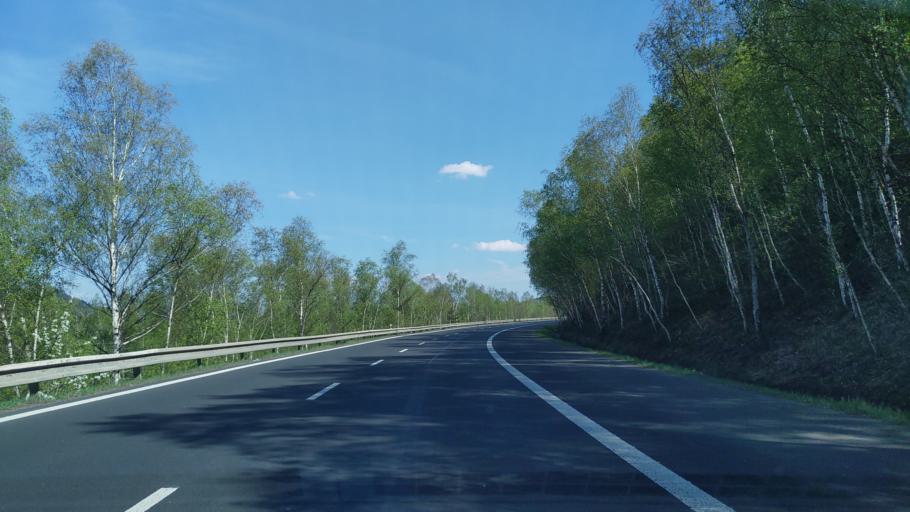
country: CZ
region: Ustecky
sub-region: Okres Most
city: Most
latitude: 50.5231
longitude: 13.6361
